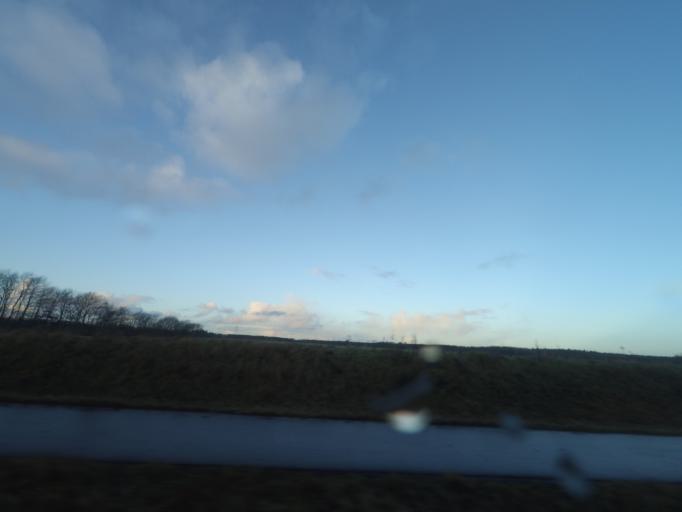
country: DK
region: Central Jutland
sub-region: Herning Kommune
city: Lind
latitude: 56.0118
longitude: 9.0377
